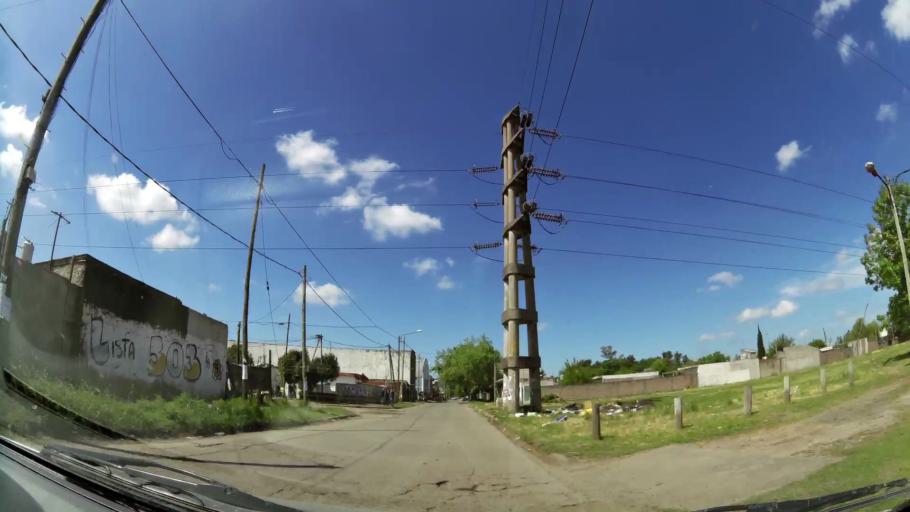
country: AR
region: Buenos Aires
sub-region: Partido de Quilmes
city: Quilmes
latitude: -34.8211
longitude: -58.2663
